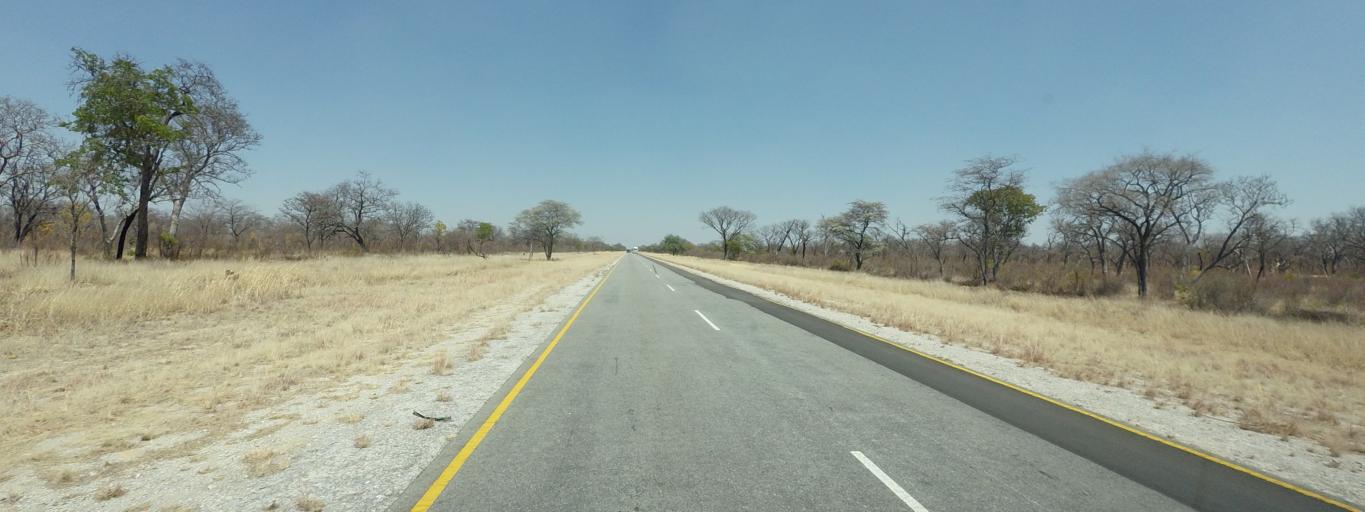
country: BW
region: North West
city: Shakawe
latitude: -18.0557
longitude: 22.0799
